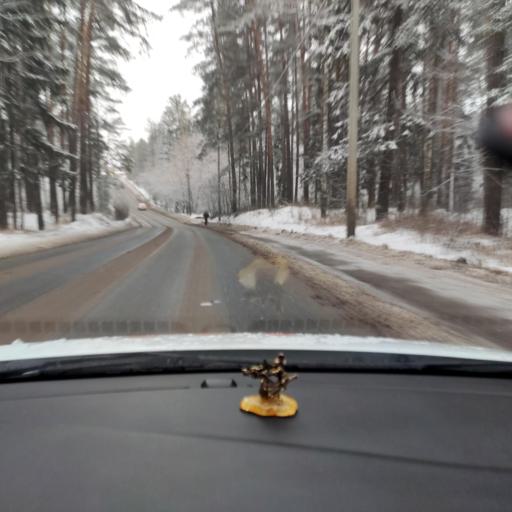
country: RU
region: Tatarstan
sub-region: Zelenodol'skiy Rayon
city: Zelenodolsk
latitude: 55.8620
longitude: 48.5344
